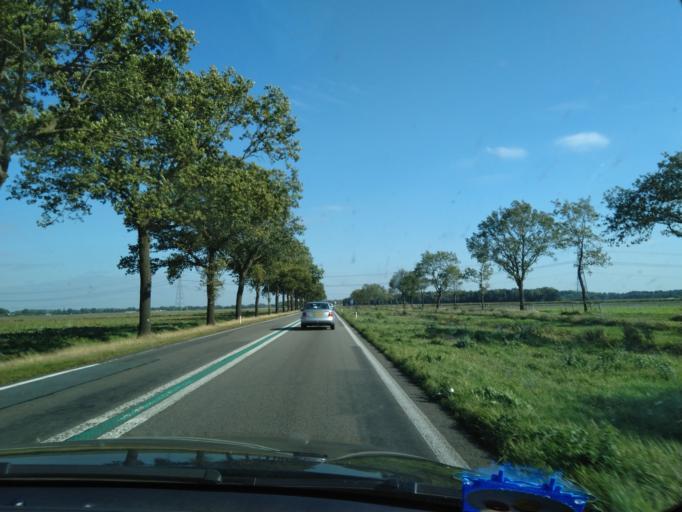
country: NL
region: Groningen
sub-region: Gemeente Veendam
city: Veendam
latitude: 53.0900
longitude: 6.9411
